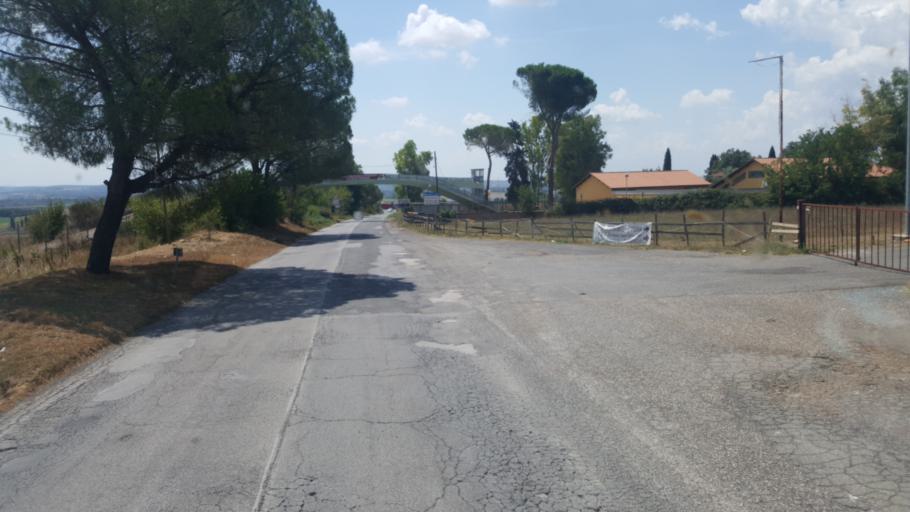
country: IT
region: Latium
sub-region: Citta metropolitana di Roma Capitale
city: Bivio di Capanelle
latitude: 42.1330
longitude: 12.5979
